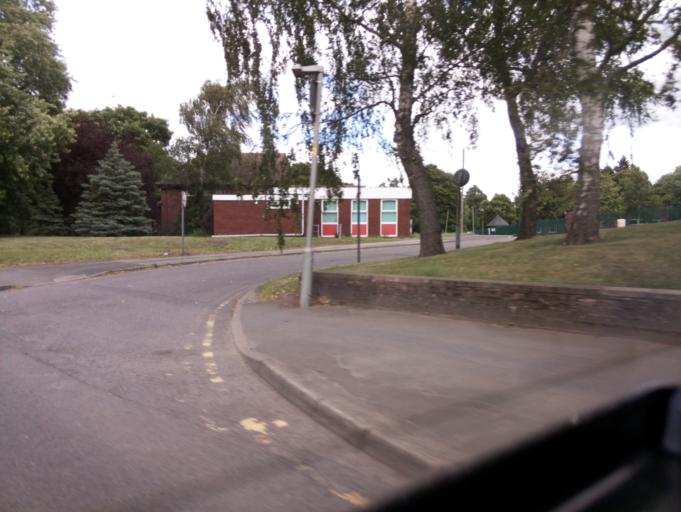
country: GB
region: England
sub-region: Warwickshire
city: Nuneaton
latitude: 52.5180
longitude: -1.4671
